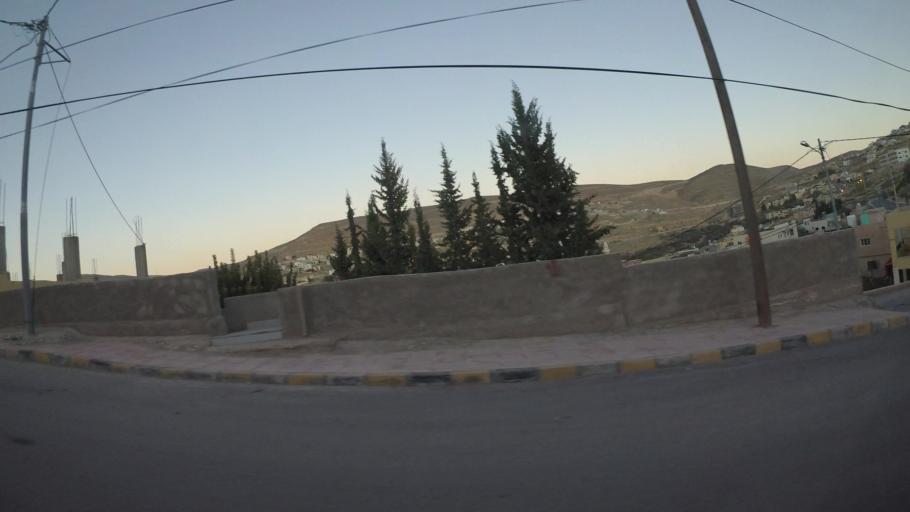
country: JO
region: Ma'an
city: Petra
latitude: 30.3160
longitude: 35.4756
